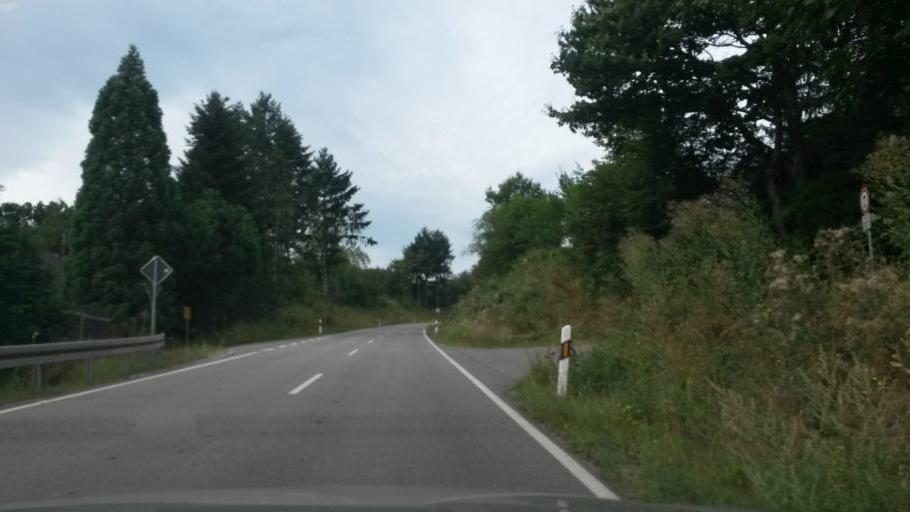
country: DE
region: Baden-Wuerttemberg
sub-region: Karlsruhe Region
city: Konigsbach-Stein
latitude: 48.9366
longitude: 8.5572
